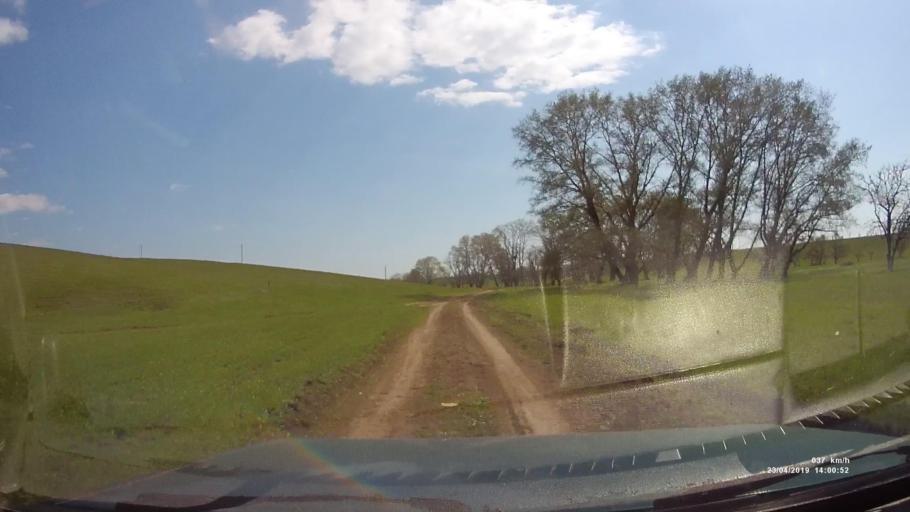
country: RU
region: Rostov
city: Remontnoye
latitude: 46.5574
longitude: 42.9474
